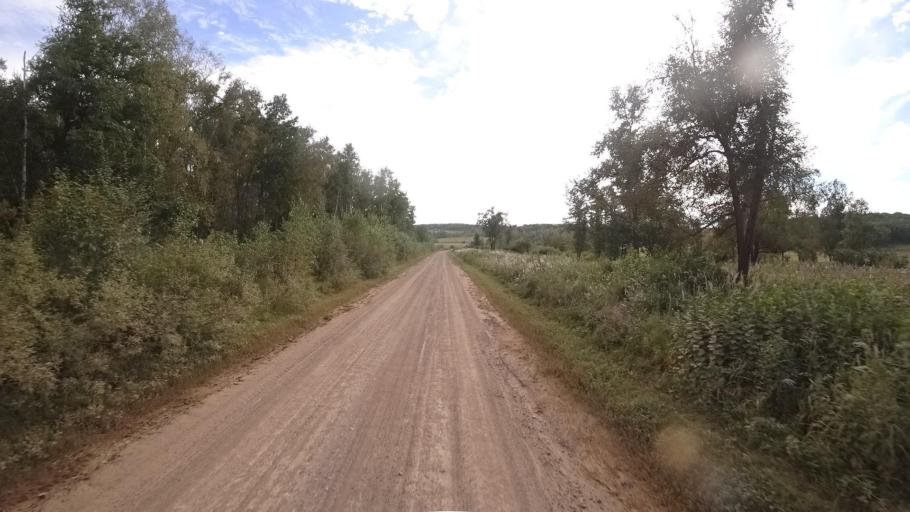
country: RU
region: Primorskiy
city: Dostoyevka
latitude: 44.3711
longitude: 133.5257
